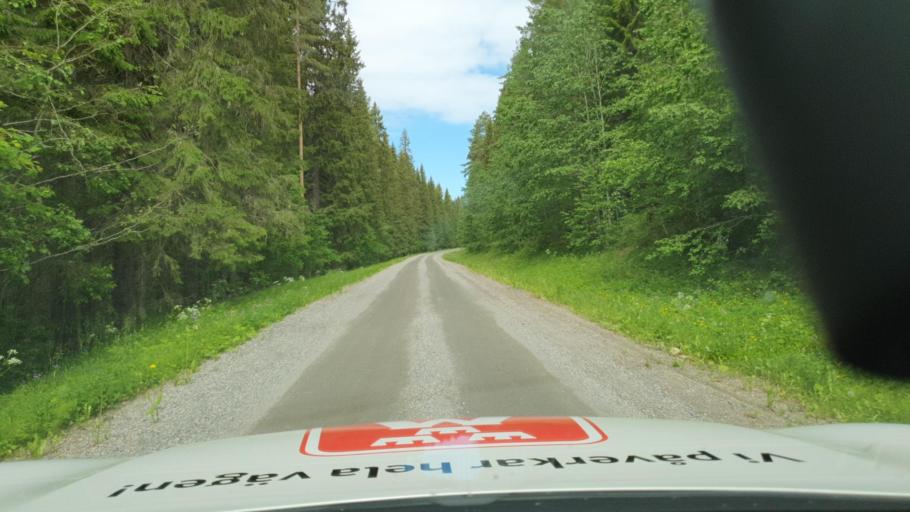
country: SE
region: Vaesterbotten
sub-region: Skelleftea Kommun
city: Forsbacka
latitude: 64.6408
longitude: 20.5433
